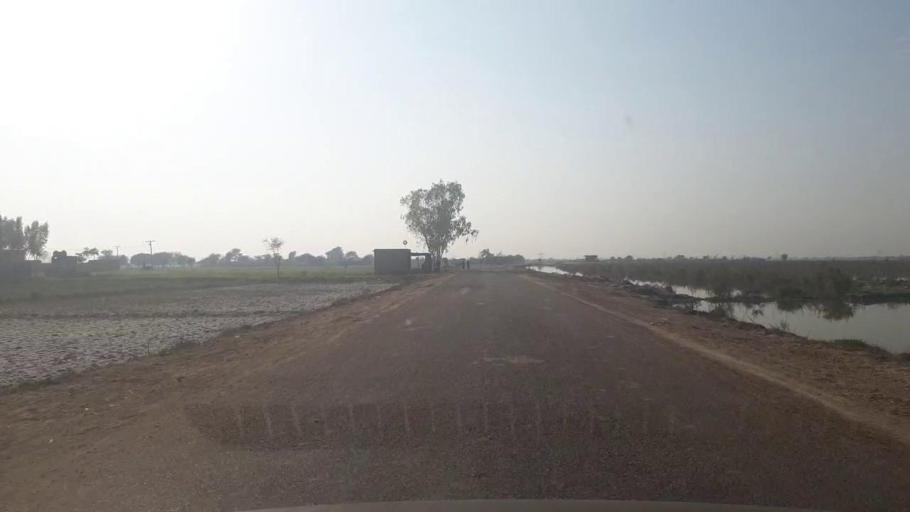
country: PK
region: Sindh
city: Sakrand
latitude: 26.0516
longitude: 68.3743
